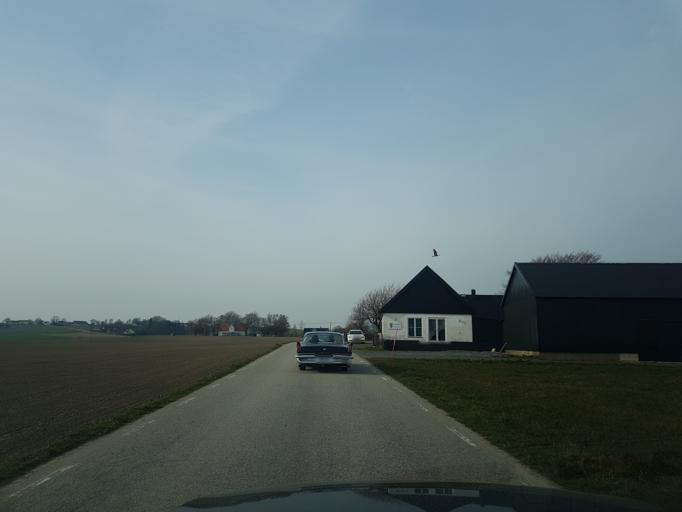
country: SE
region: Skane
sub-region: Ystads Kommun
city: Ystad
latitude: 55.4606
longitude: 13.8256
